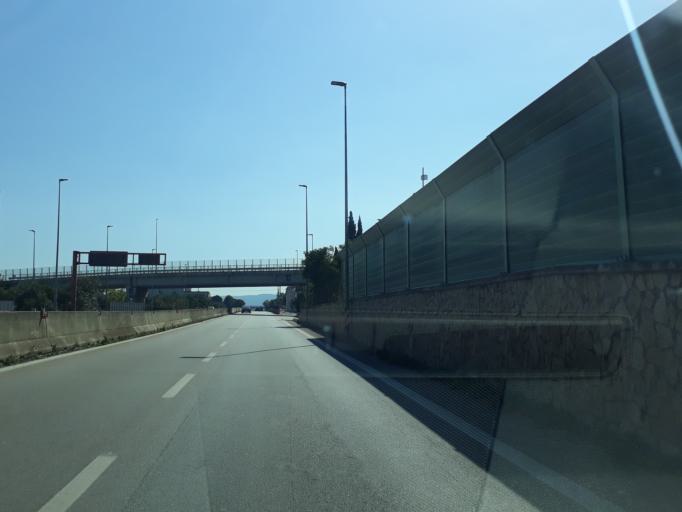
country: IT
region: Apulia
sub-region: Provincia di Brindisi
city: Fasano
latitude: 40.8813
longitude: 17.3377
